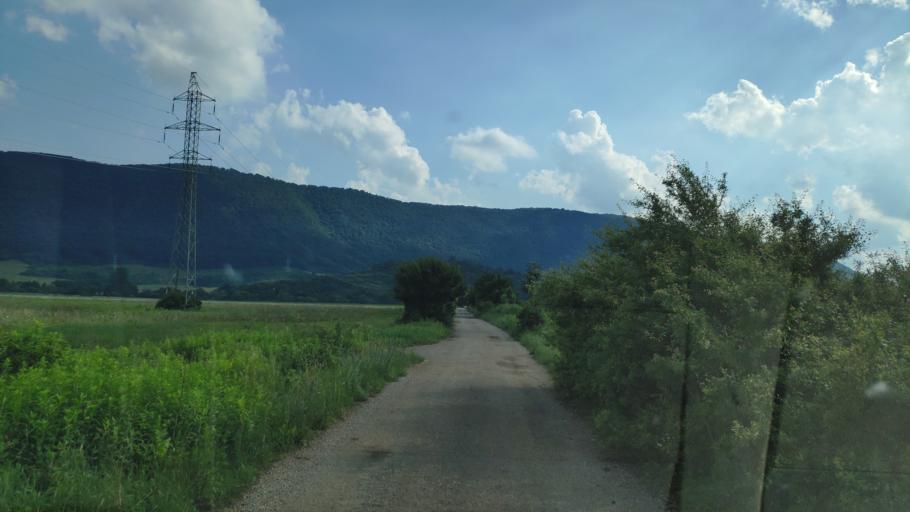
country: SK
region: Kosicky
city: Medzev
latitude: 48.5965
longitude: 20.7328
